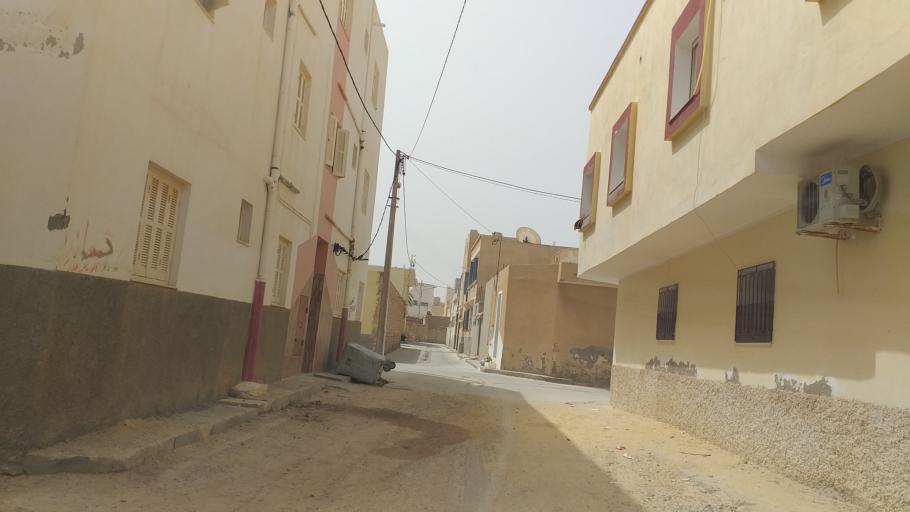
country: TN
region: Qabis
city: Gabes
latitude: 33.9418
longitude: 10.0616
